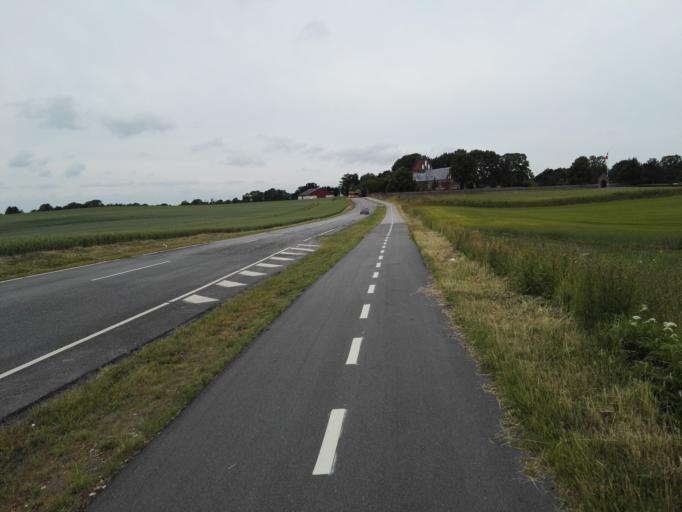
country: DK
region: Capital Region
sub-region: Egedal Kommune
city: Smorumnedre
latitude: 55.7324
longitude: 12.2816
